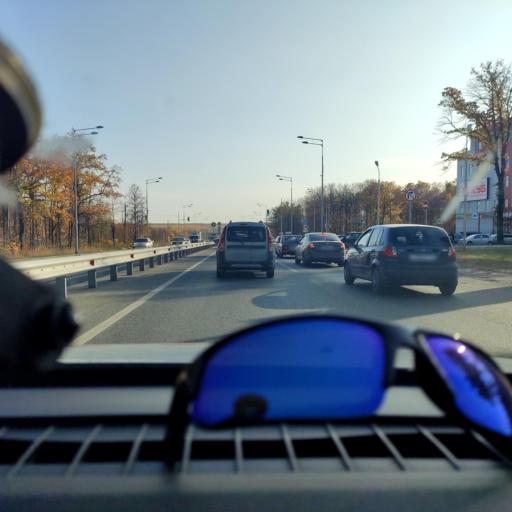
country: RU
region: Samara
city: Novosemeykino
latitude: 53.3478
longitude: 50.2334
